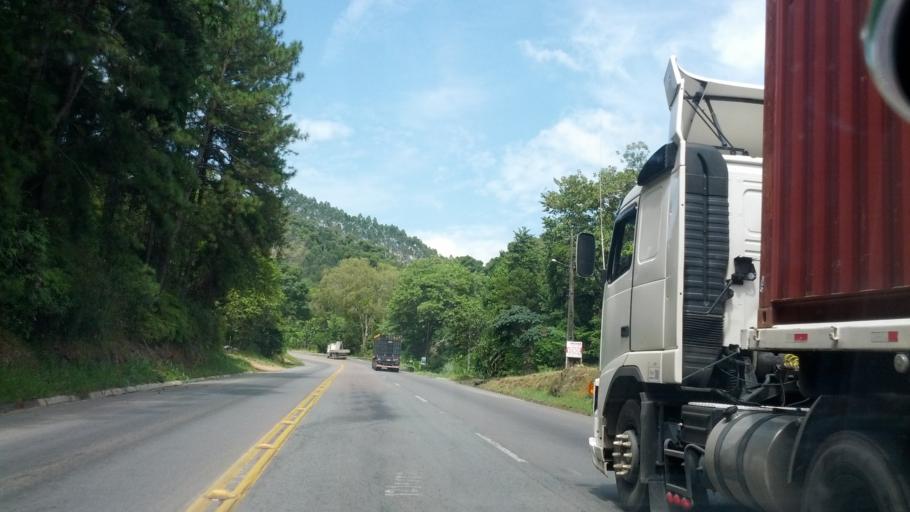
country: BR
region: Santa Catarina
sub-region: Ibirama
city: Ibirama
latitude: -27.0887
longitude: -49.5195
